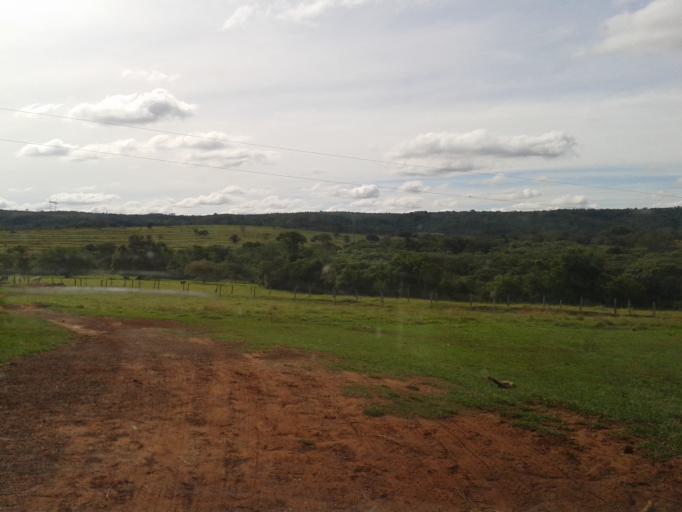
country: BR
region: Minas Gerais
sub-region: Campina Verde
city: Campina Verde
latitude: -19.4298
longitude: -49.7138
